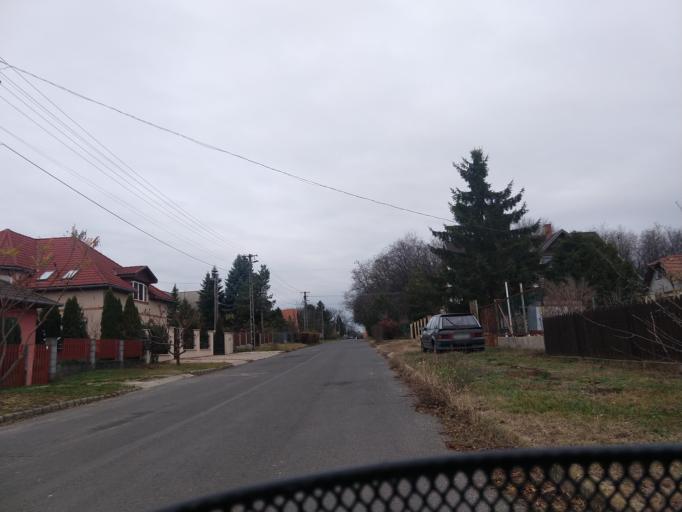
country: HU
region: Pest
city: Orbottyan
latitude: 47.6718
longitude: 19.2879
